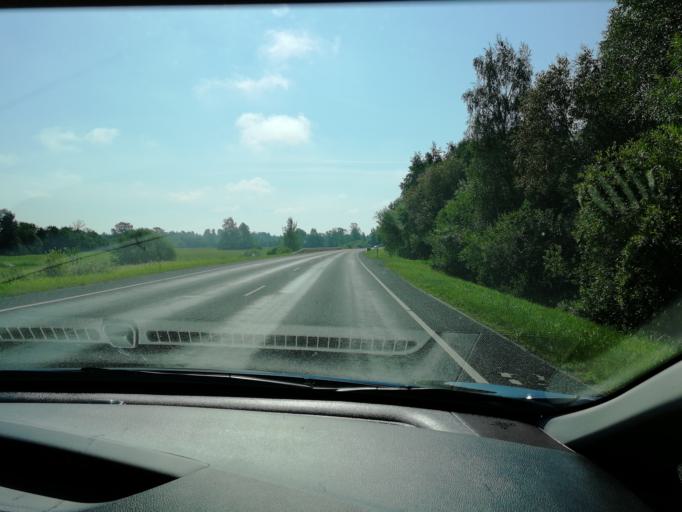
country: EE
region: Paernumaa
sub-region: Saarde vald
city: Kilingi-Nomme
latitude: 58.1900
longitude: 24.7790
